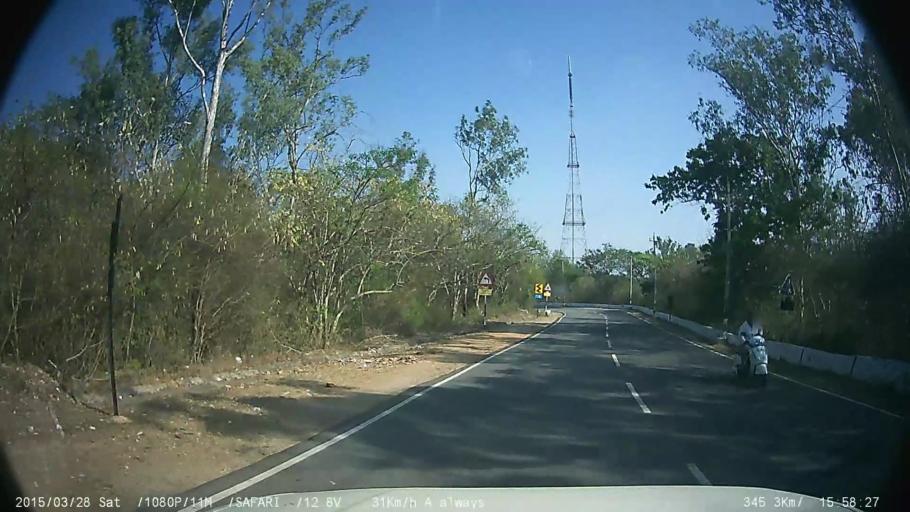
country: IN
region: Karnataka
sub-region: Mysore
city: Mysore
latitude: 12.2766
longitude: 76.6742
